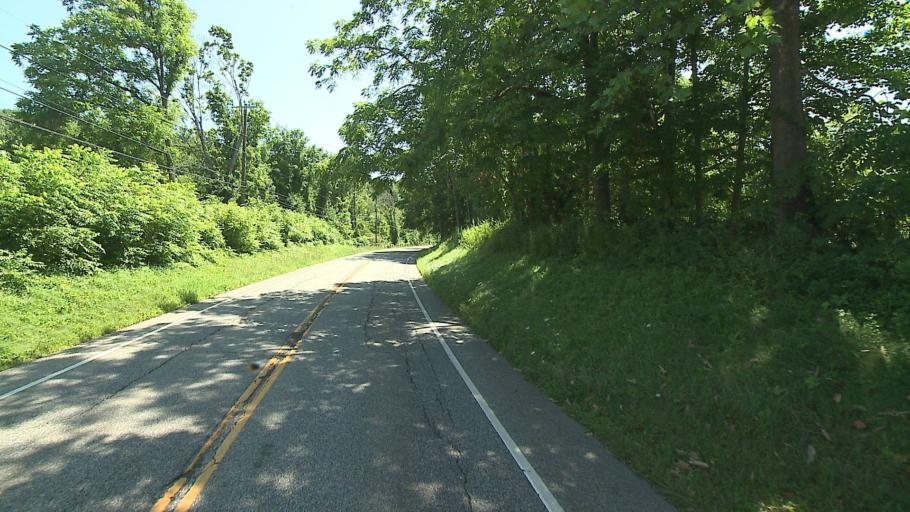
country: US
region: Connecticut
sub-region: Litchfield County
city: Kent
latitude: 41.8548
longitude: -73.4490
